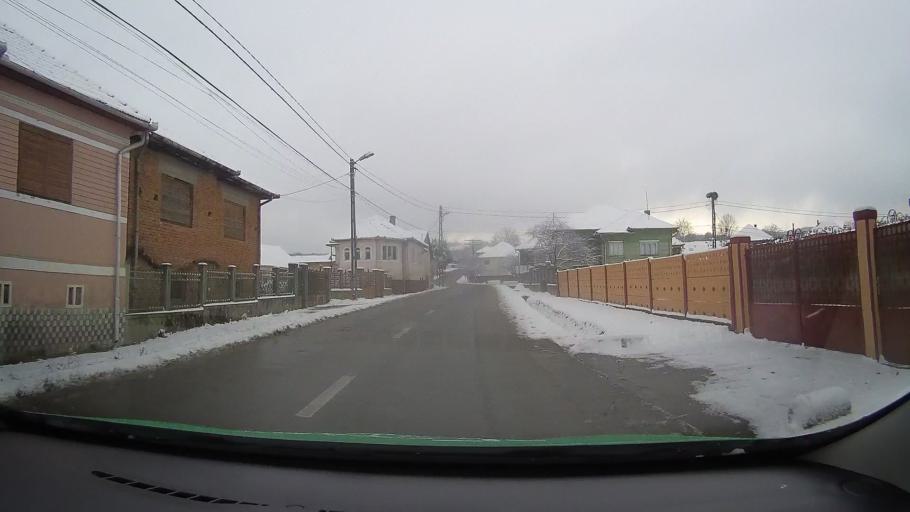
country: RO
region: Hunedoara
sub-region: Oras Hateg
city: Hateg
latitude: 45.6521
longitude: 22.9257
